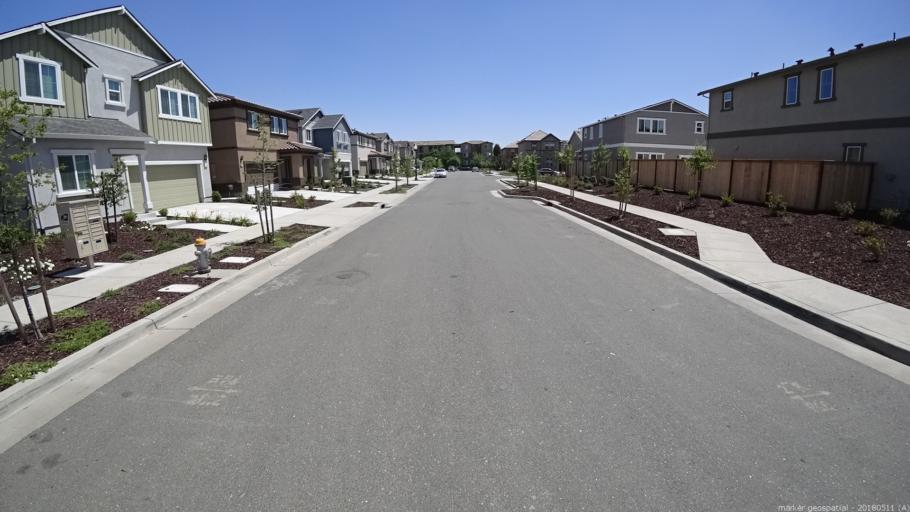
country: US
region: California
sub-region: Sacramento County
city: Rio Linda
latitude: 38.6556
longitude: -121.4988
